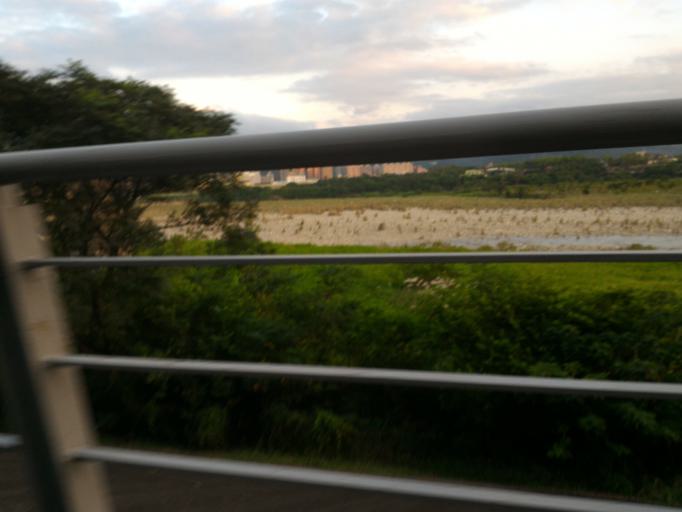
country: TW
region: Taipei
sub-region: Taipei
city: Banqiao
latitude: 24.9693
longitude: 121.4068
